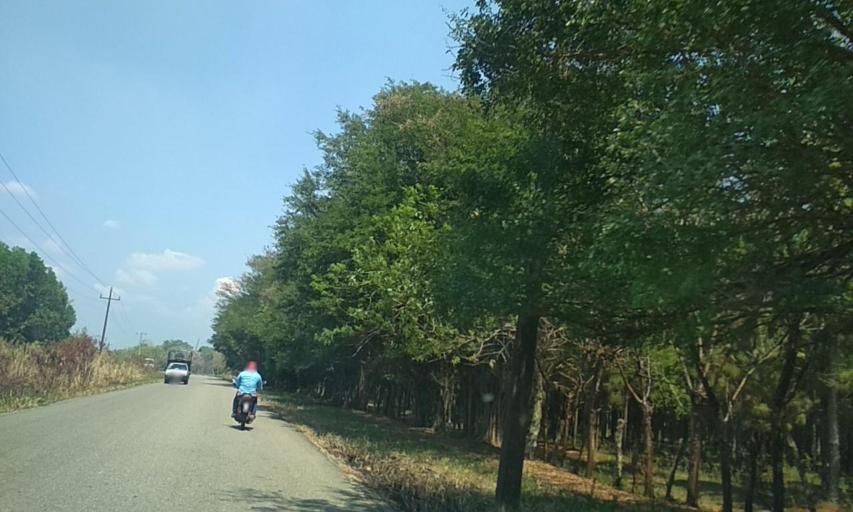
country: MX
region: Tabasco
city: Huimanguillo
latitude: 17.7998
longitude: -93.4669
